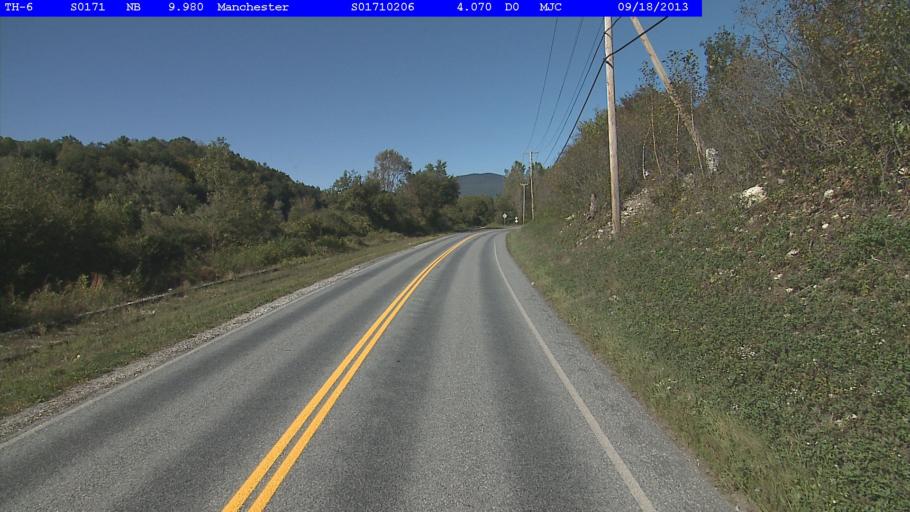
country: US
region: Vermont
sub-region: Bennington County
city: Manchester Center
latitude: 43.1628
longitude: -73.0542
